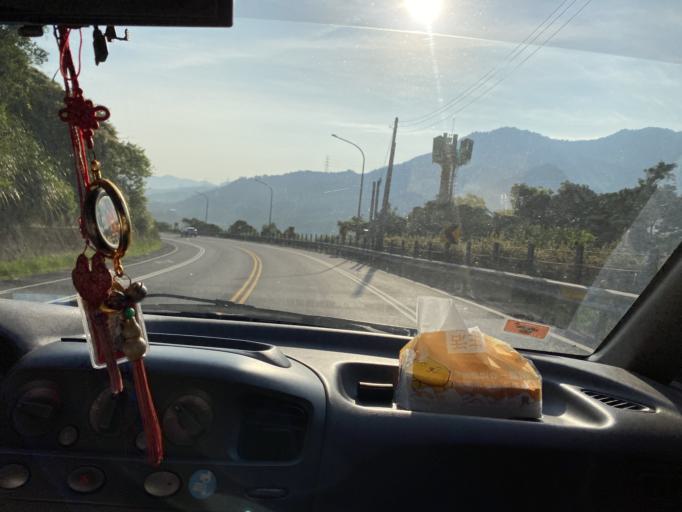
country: TW
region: Taiwan
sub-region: Keelung
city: Keelung
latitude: 25.0165
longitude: 121.8003
